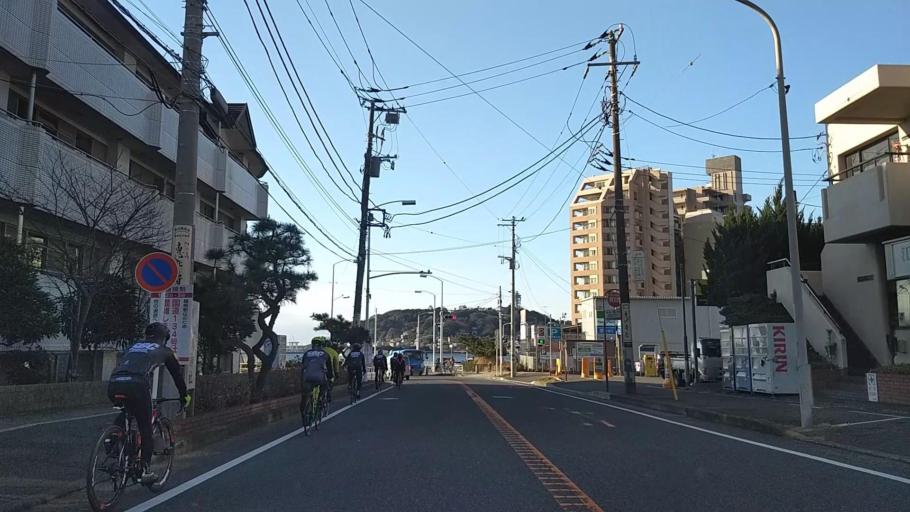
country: JP
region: Kanagawa
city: Fujisawa
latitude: 35.3089
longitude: 139.4875
